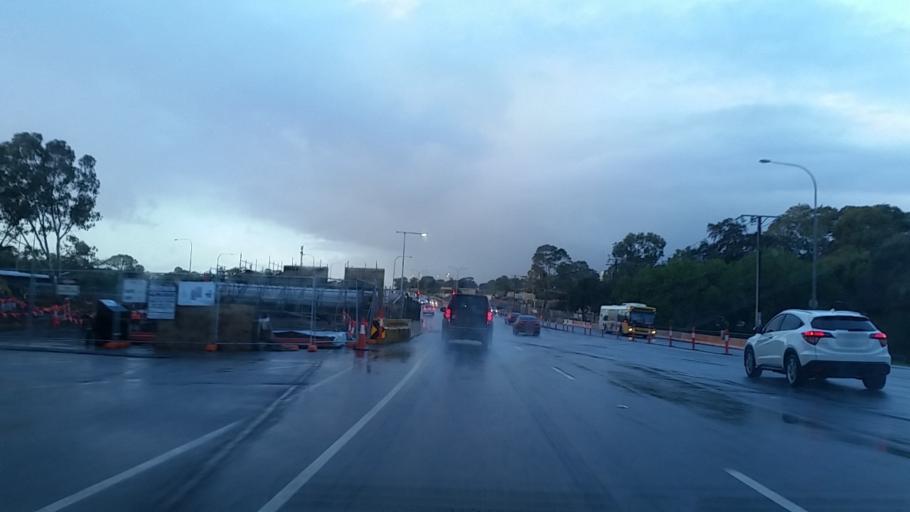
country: AU
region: South Australia
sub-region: Marion
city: Marion
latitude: -35.0237
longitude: 138.5622
